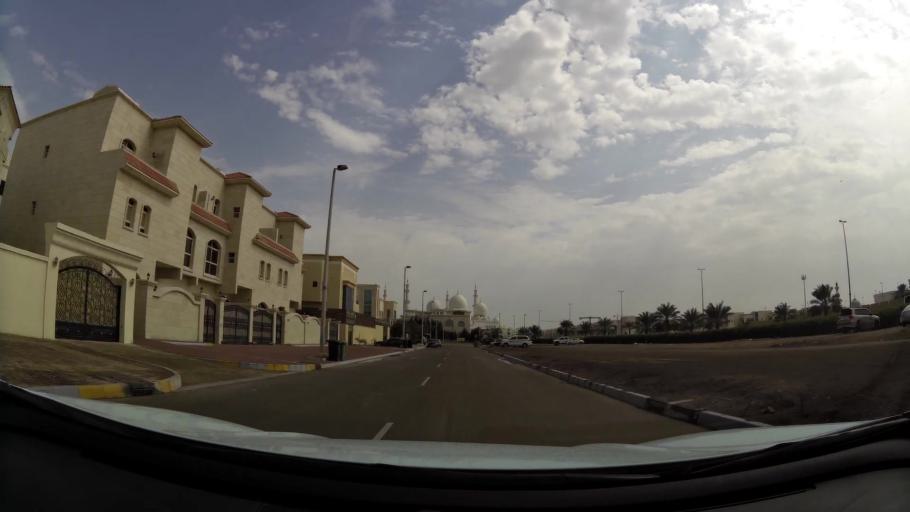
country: AE
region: Abu Dhabi
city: Abu Dhabi
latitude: 24.4144
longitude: 54.4667
